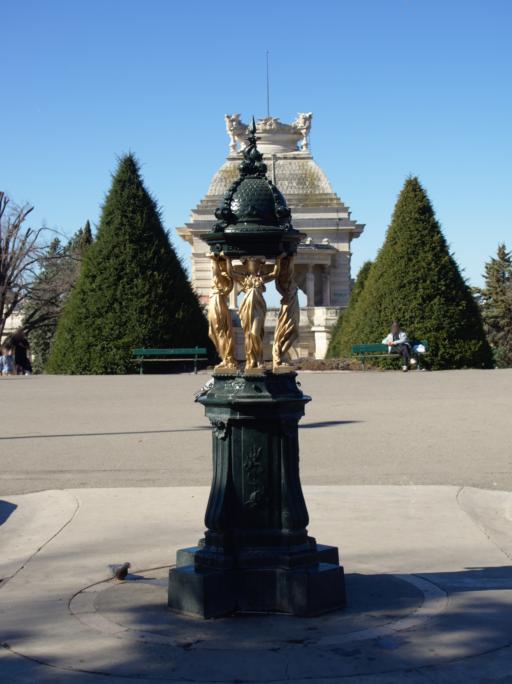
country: FR
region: Provence-Alpes-Cote d'Azur
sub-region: Departement des Bouches-du-Rhone
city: Marseille 04
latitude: 43.3048
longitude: 5.3956
